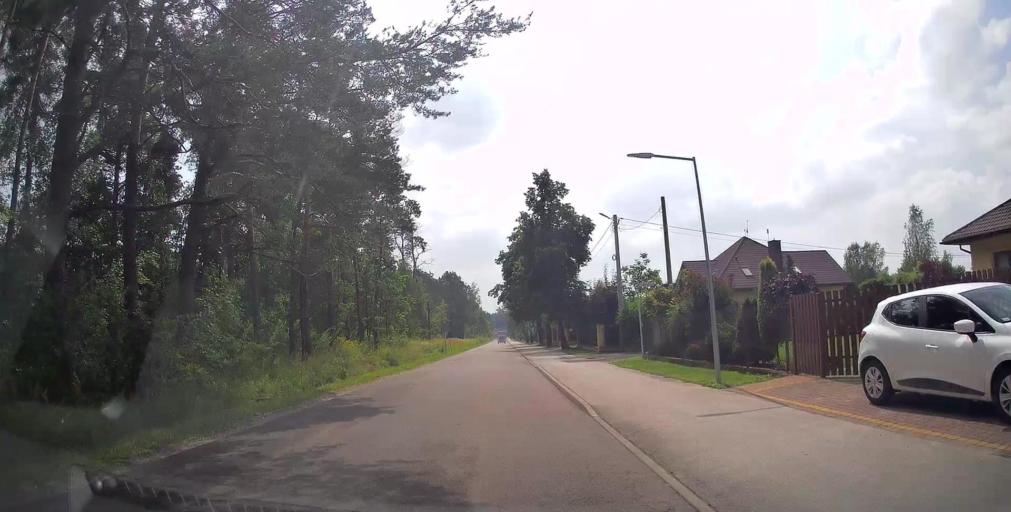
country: PL
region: Masovian Voivodeship
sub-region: Powiat bialobrzeski
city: Sucha
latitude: 51.6275
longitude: 20.9536
